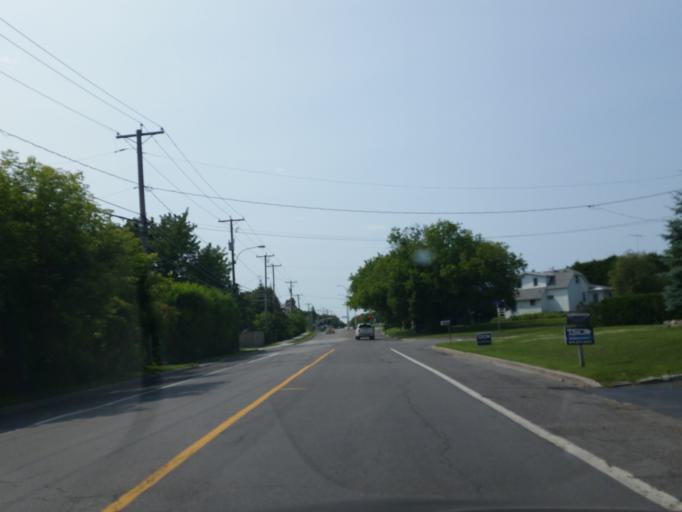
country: CA
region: Ontario
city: Bells Corners
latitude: 45.4059
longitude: -75.8623
